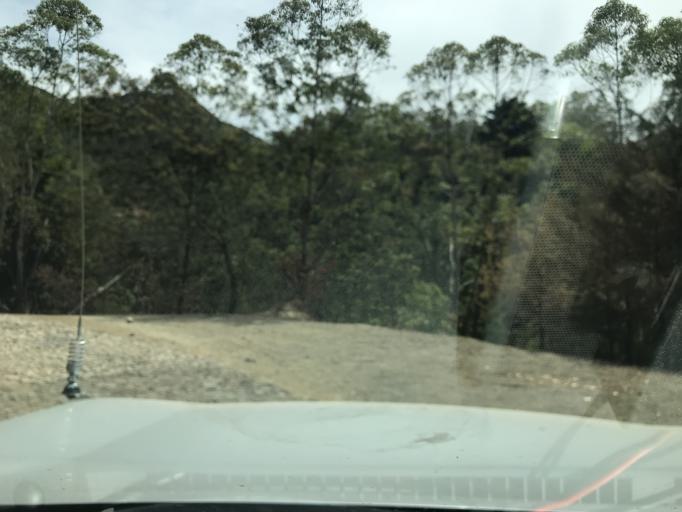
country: TL
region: Ainaro
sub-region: Ainaro
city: Ainaro
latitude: -8.8822
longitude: 125.5284
